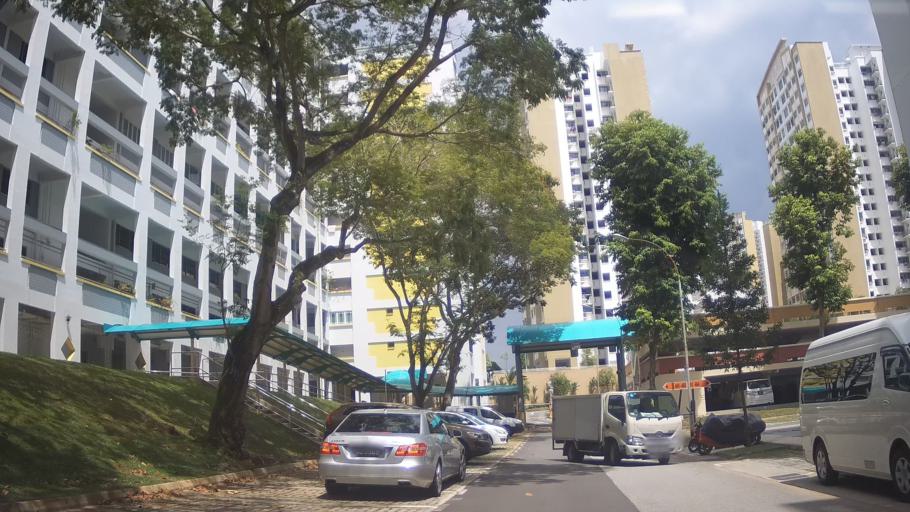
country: MY
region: Johor
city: Johor Bahru
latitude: 1.3816
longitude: 103.7684
